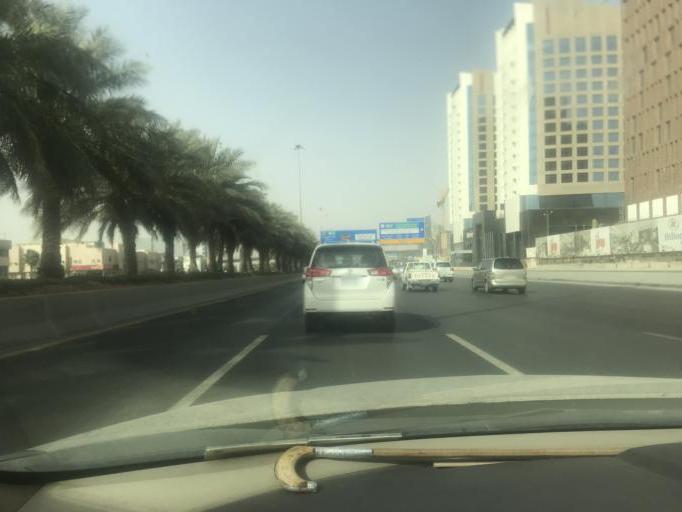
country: SA
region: Ar Riyad
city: Riyadh
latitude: 24.7644
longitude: 46.6560
